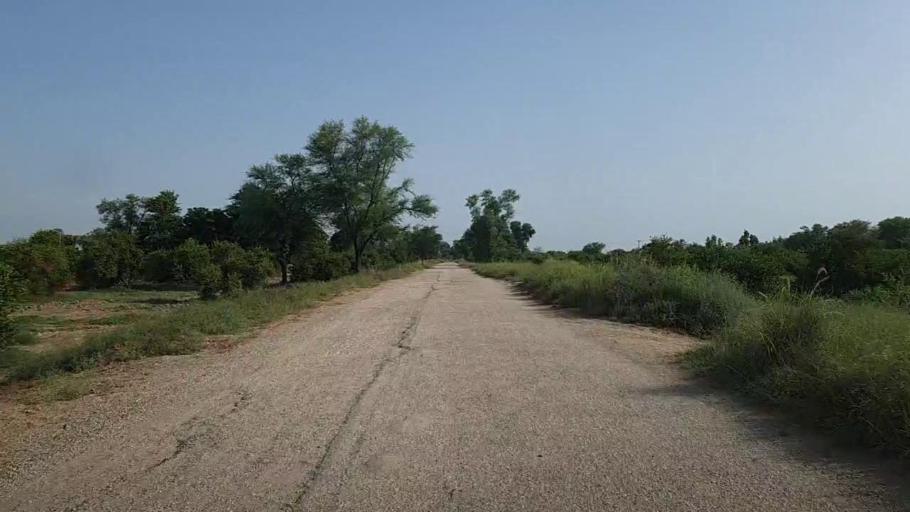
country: PK
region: Sindh
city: Karaundi
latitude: 26.8598
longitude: 68.3309
